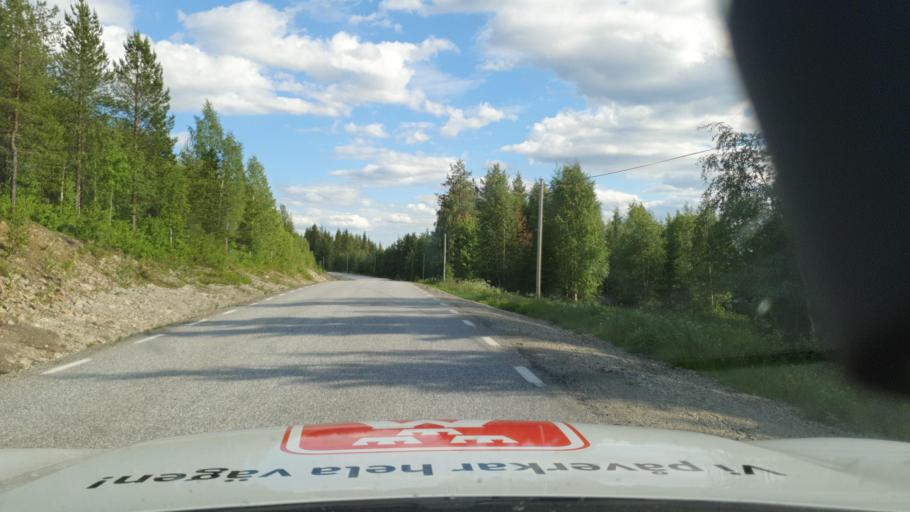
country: SE
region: Vaesterbotten
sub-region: Skelleftea Kommun
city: Langsele
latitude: 64.7298
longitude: 19.9545
